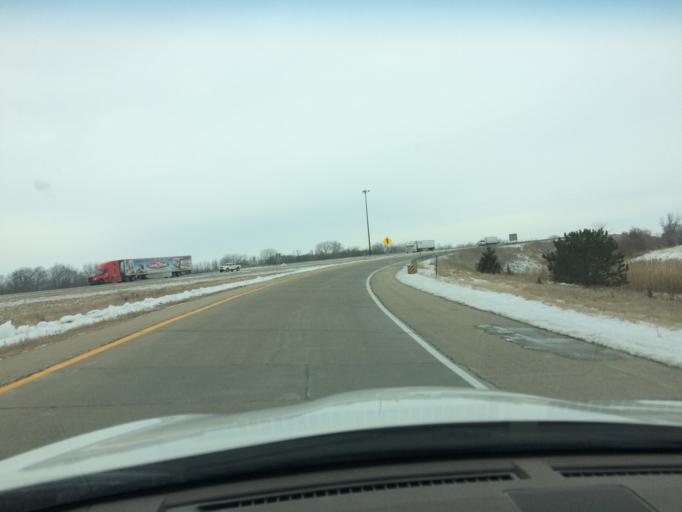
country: US
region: Illinois
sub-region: LaSalle County
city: Mendota
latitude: 41.4722
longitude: -89.0491
